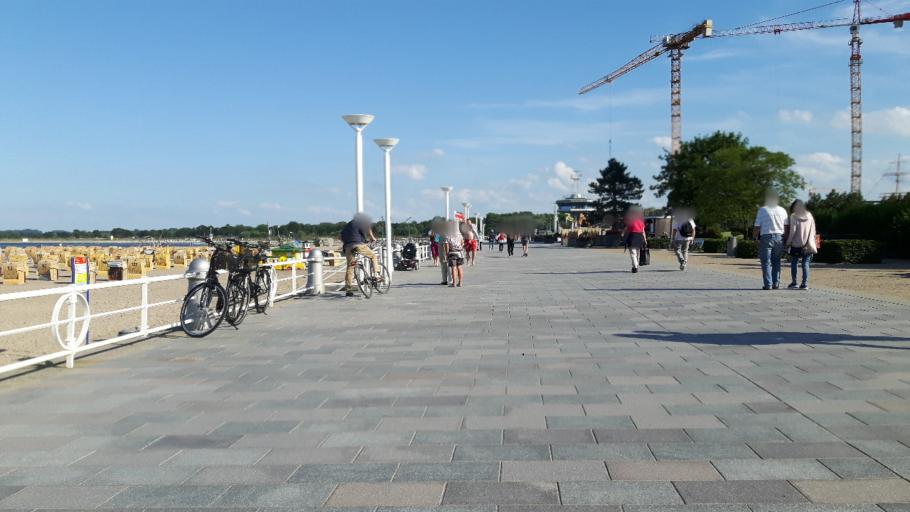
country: DE
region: Schleswig-Holstein
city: Travemuende
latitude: 53.9630
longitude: 10.8822
